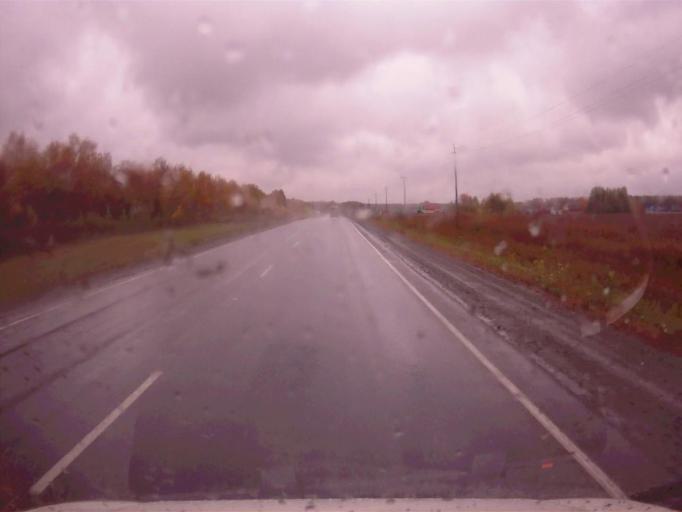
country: RU
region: Chelyabinsk
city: Argayash
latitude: 55.4052
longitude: 61.0616
